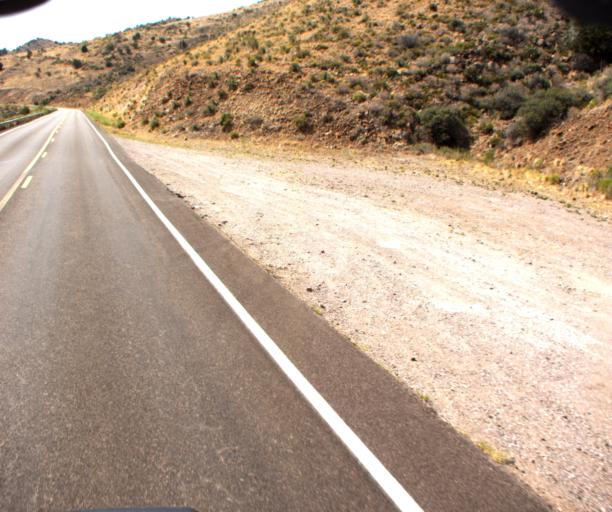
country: US
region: Arizona
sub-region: Greenlee County
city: Clifton
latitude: 33.0499
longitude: -109.0970
